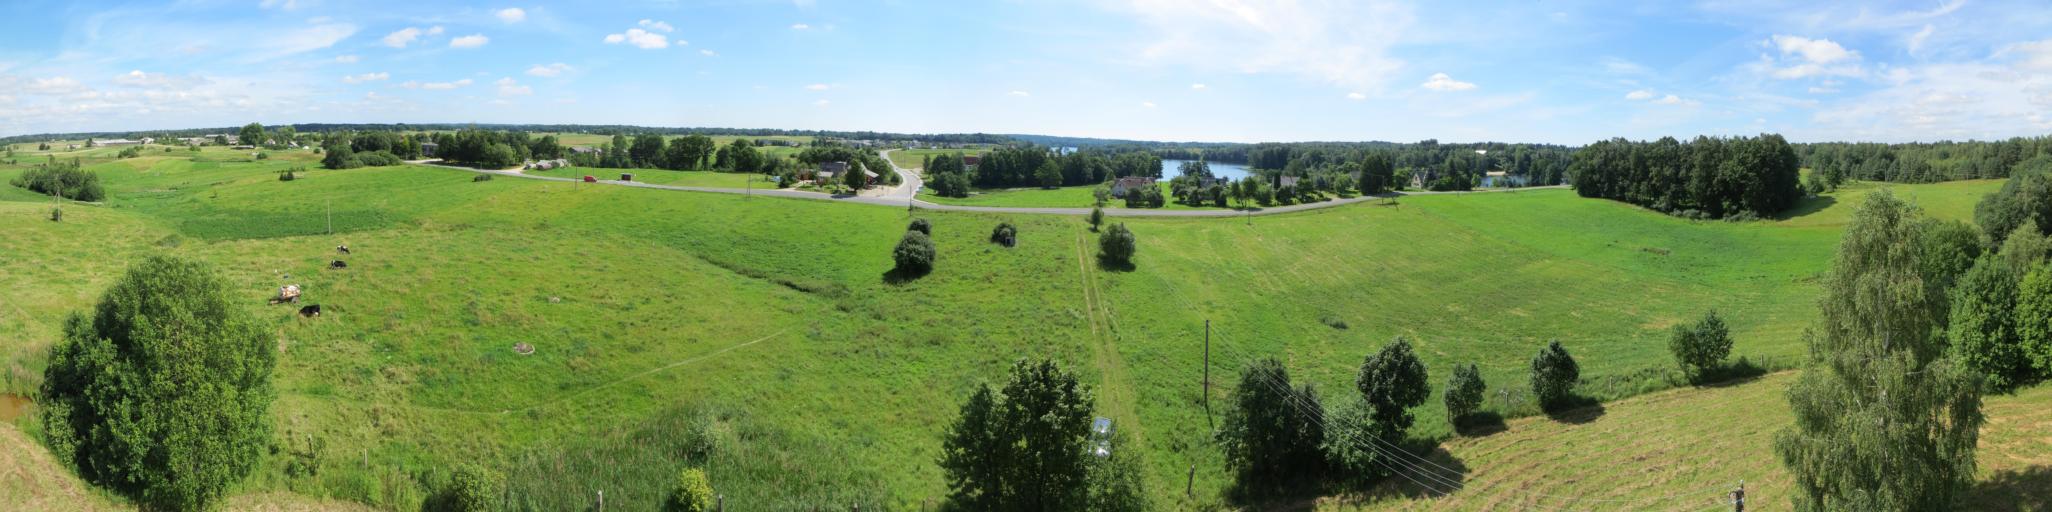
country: LT
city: Moletai
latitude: 55.1659
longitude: 25.3110
